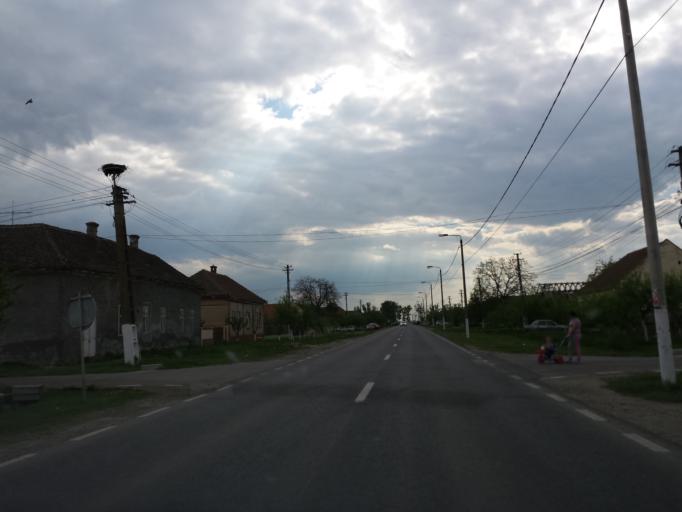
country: RO
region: Timis
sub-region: Comuna Cenad
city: Cenad
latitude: 46.1320
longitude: 20.5724
